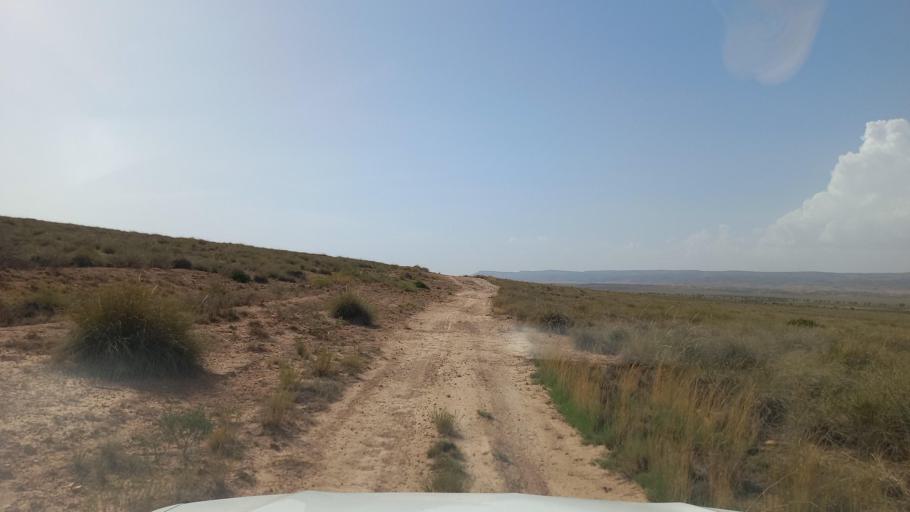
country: TN
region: Al Qasrayn
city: Kasserine
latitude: 35.2150
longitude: 8.9882
